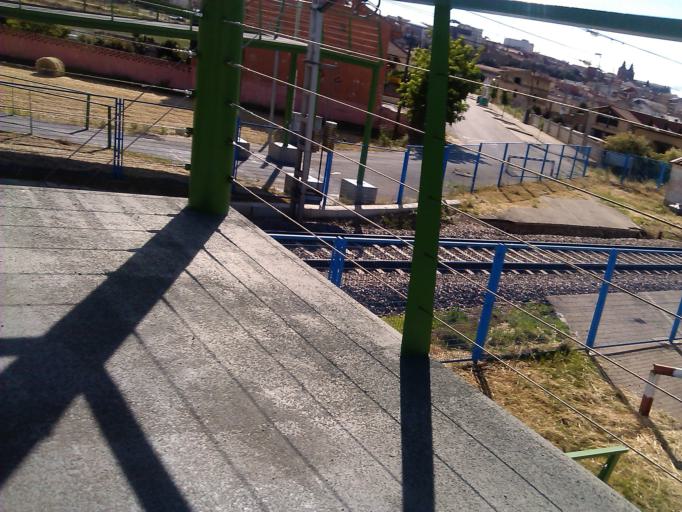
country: ES
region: Castille and Leon
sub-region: Provincia de Leon
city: Astorga
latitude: 42.4547
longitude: -6.0447
